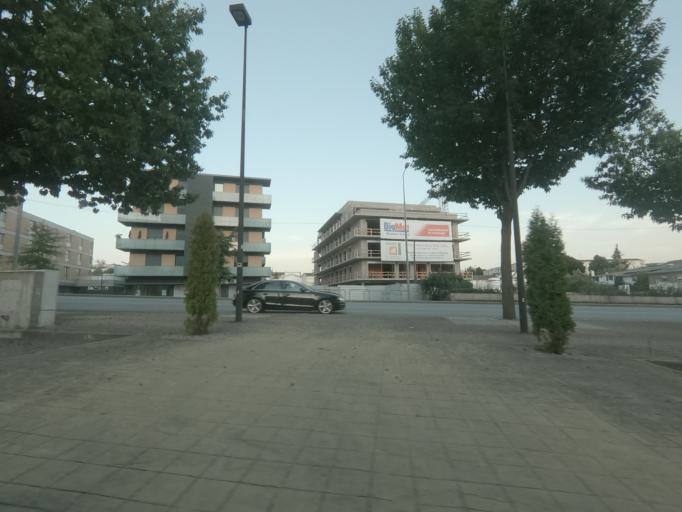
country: PT
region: Vila Real
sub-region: Vila Real
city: Vila Real
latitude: 41.2956
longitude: -7.7320
